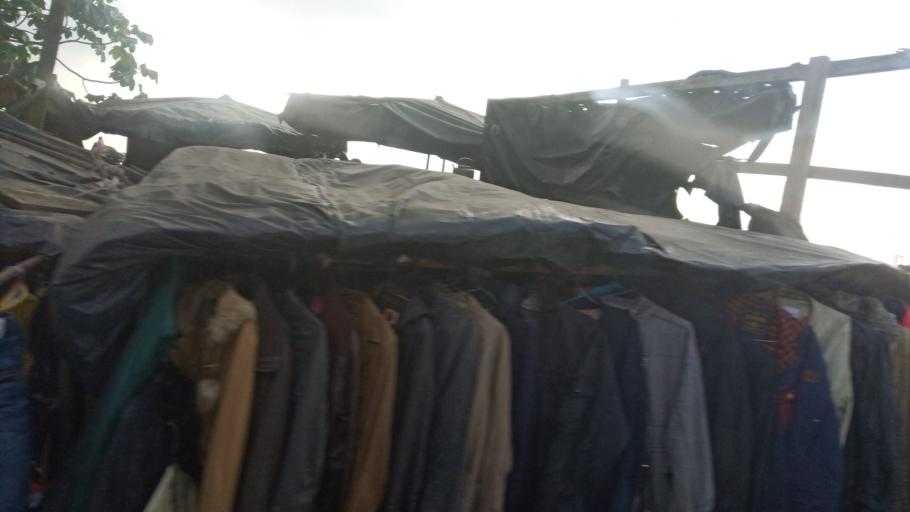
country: CI
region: Lagunes
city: Abidjan
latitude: 5.3594
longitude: -4.0287
